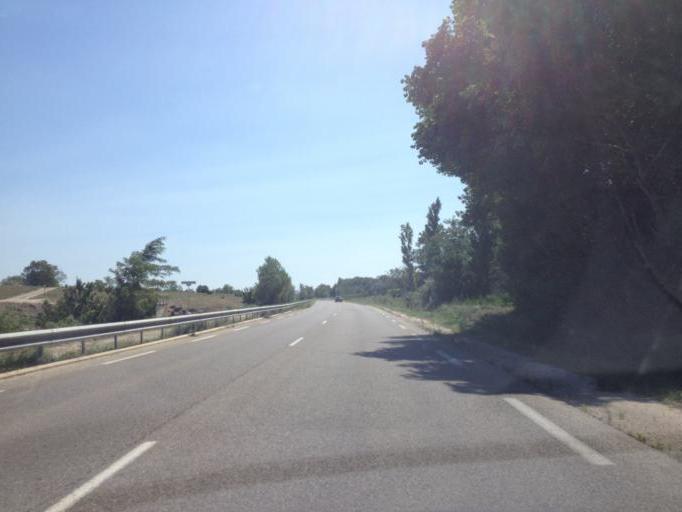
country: FR
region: Languedoc-Roussillon
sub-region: Departement du Gard
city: Roquemaure
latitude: 44.0489
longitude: 4.7873
